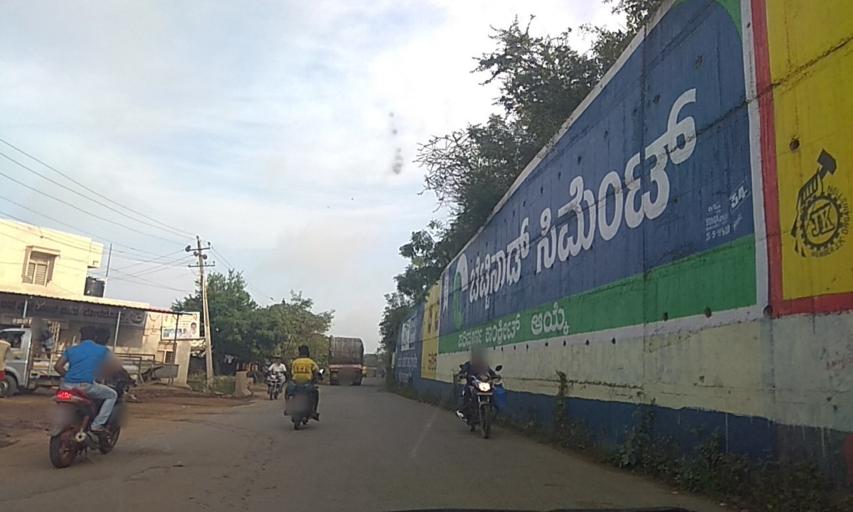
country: IN
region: Karnataka
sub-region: Haveri
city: Byadgi
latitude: 14.7185
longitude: 75.4816
